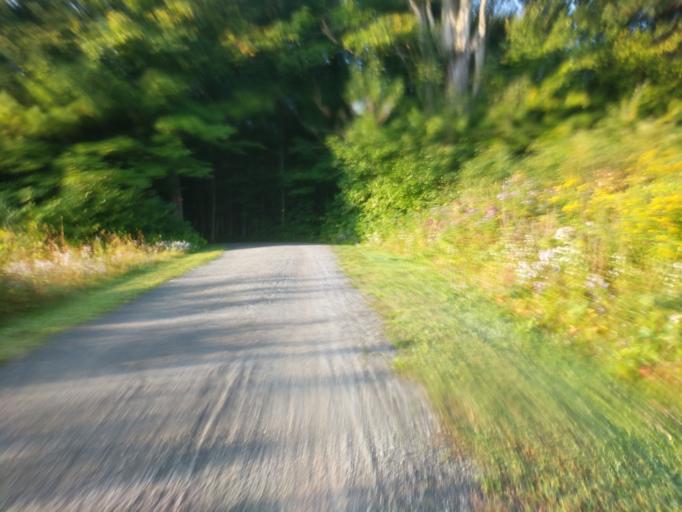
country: CA
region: Ontario
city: Bells Corners
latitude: 45.3251
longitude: -75.8588
